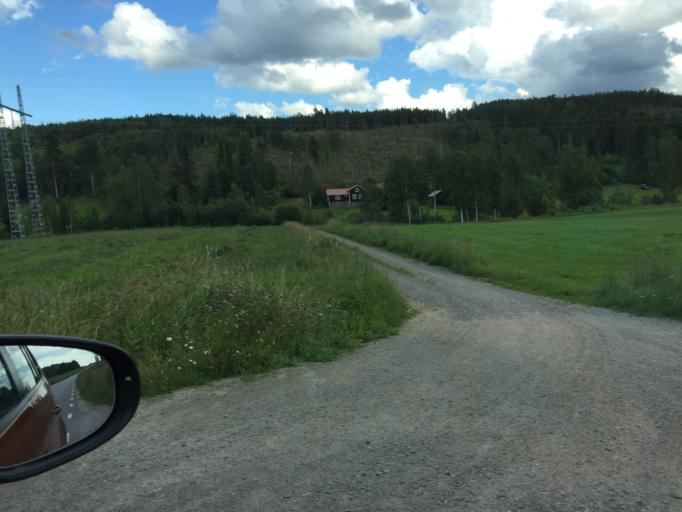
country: SE
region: Gaevleborg
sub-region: Ljusdals Kommun
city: Jaervsoe
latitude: 61.7260
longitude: 16.2870
